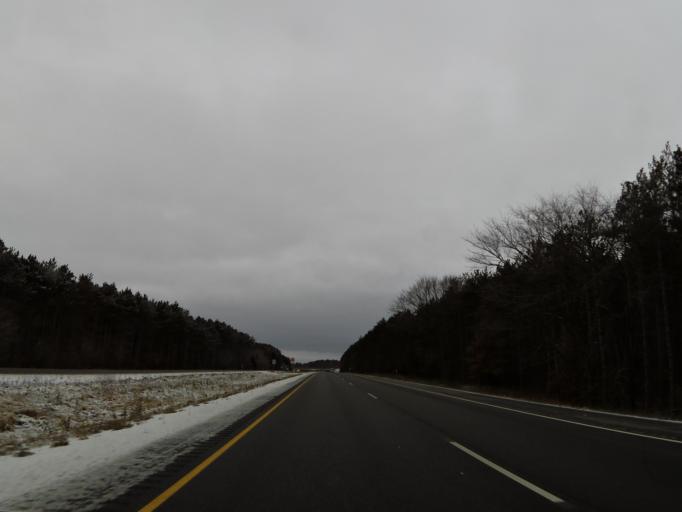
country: US
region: Wisconsin
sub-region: Eau Claire County
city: Altoona
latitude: 44.7587
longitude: -91.3979
